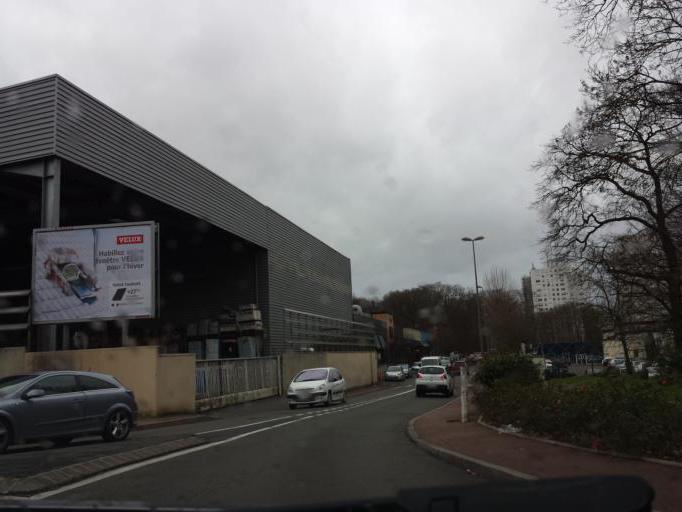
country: FR
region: Ile-de-France
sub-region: Departement du Val-d'Oise
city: Montigny-les-Cormeilles
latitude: 48.9906
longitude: 2.2087
